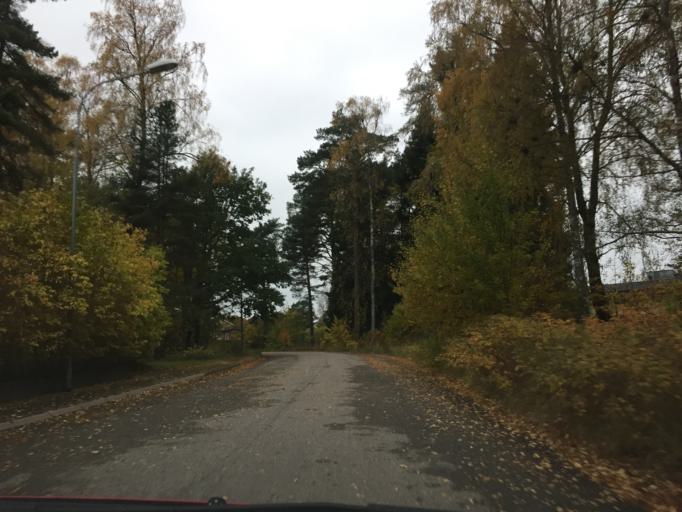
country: SE
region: Vaestra Goetaland
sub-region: Trollhattan
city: Trollhattan
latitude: 58.2581
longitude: 12.2897
